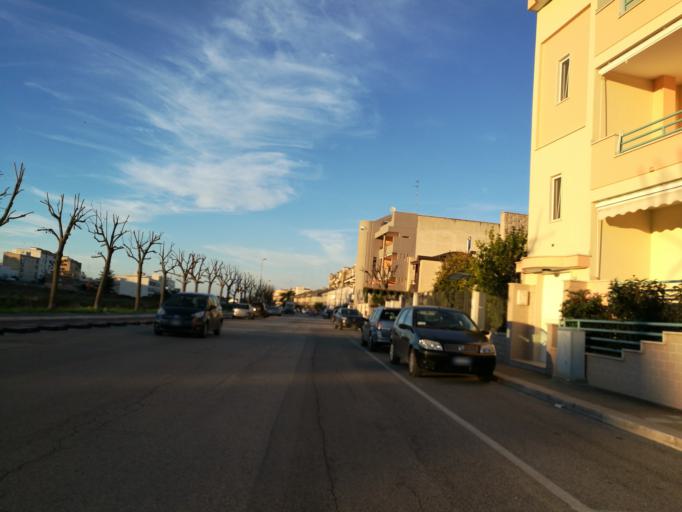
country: IT
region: Apulia
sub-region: Provincia di Bari
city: Adelfia
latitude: 41.0002
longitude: 16.8735
